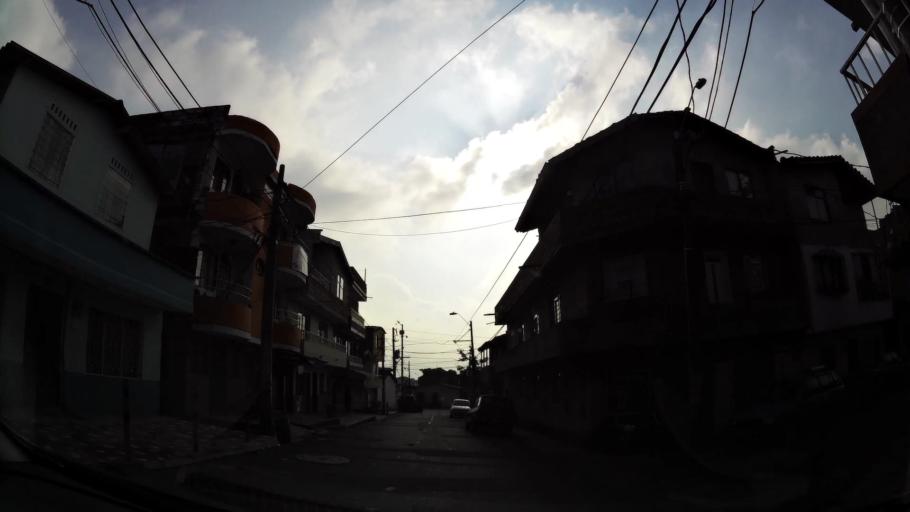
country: CO
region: Antioquia
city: Sabaneta
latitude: 6.1621
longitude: -75.6255
